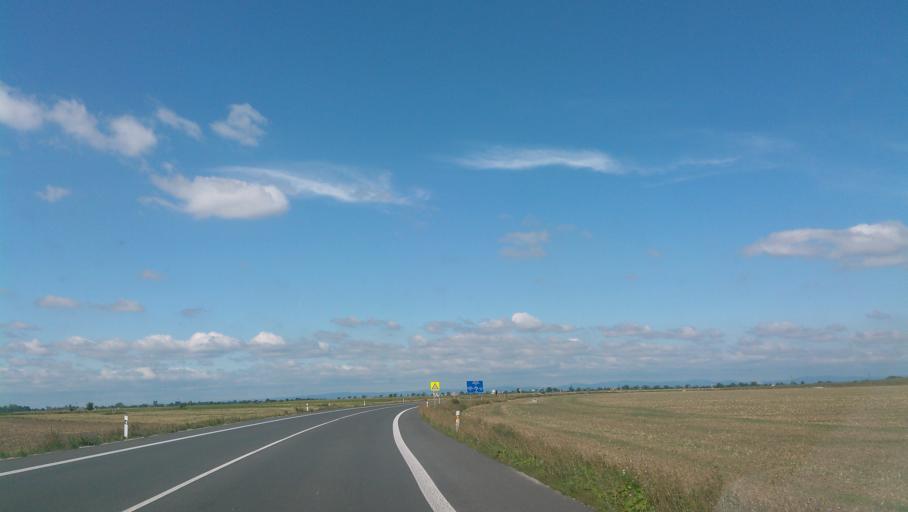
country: SK
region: Trnavsky
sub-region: Okres Galanta
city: Galanta
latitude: 48.1771
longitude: 17.7118
